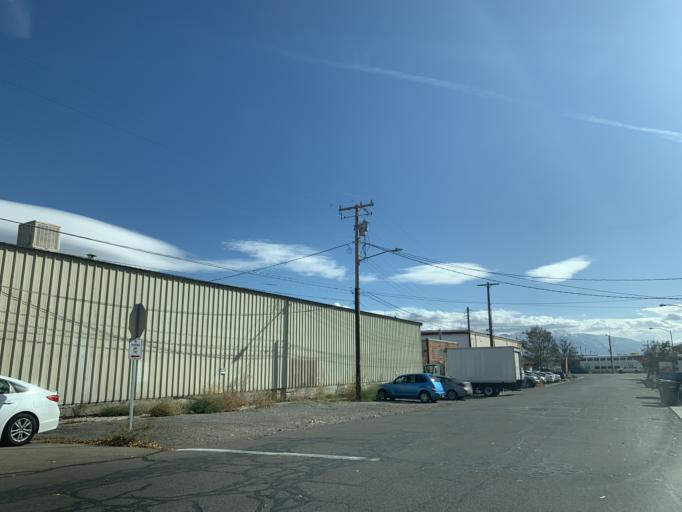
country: US
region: Utah
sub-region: Utah County
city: Provo
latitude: 40.2268
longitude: -111.6606
